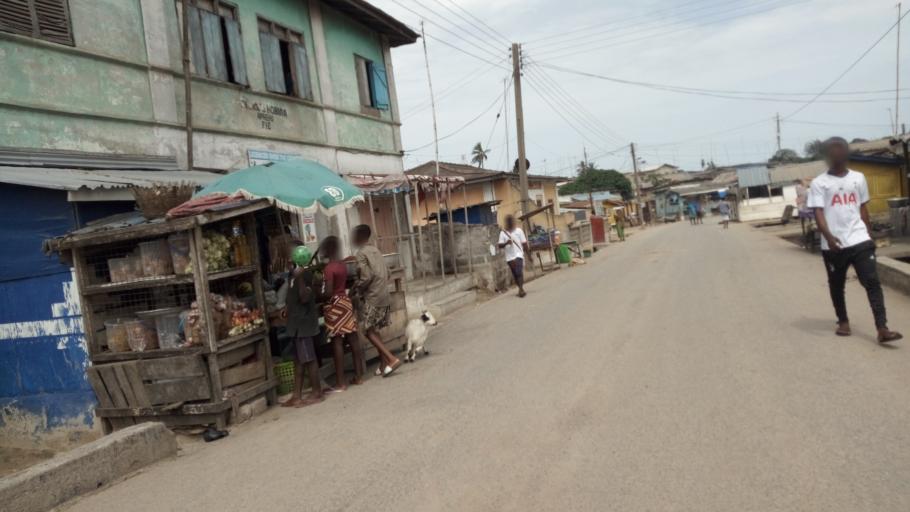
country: GH
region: Central
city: Winneba
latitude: 5.3451
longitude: -0.6192
